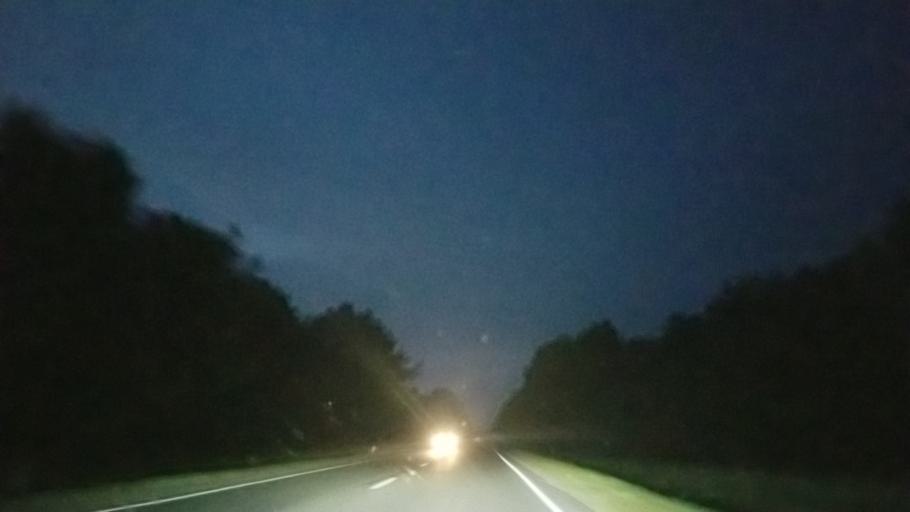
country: PL
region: Lublin Voivodeship
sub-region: Powiat bialski
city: Koden
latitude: 51.9644
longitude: 23.6850
